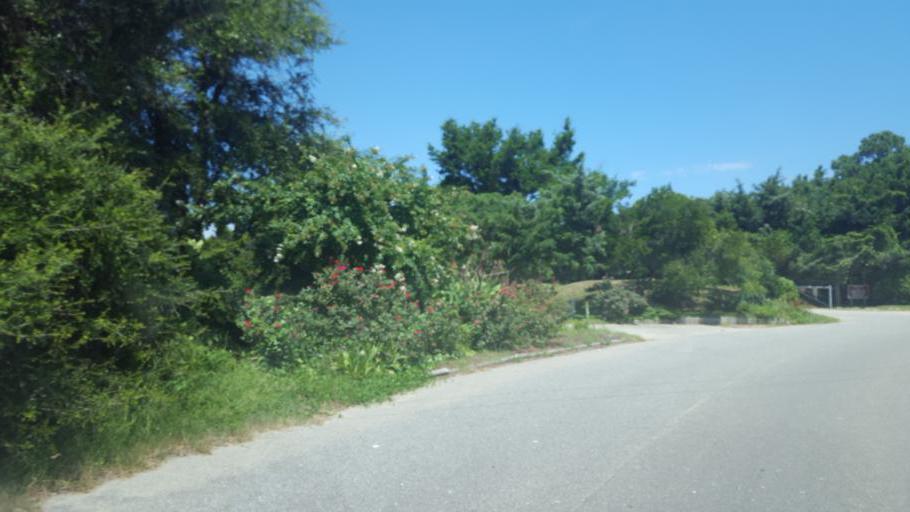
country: US
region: North Carolina
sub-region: Dare County
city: Nags Head
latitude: 35.9514
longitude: -75.6318
